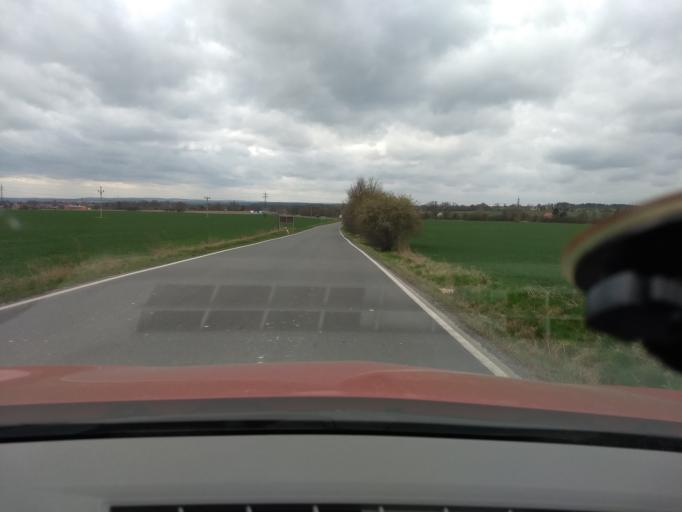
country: CZ
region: Central Bohemia
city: Unhost'
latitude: 50.0632
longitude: 14.1651
